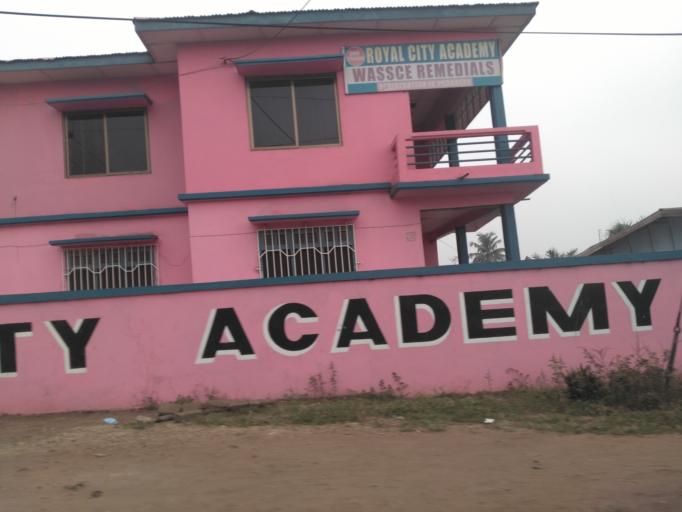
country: GH
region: Ashanti
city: Tafo
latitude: 6.7142
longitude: -1.6069
